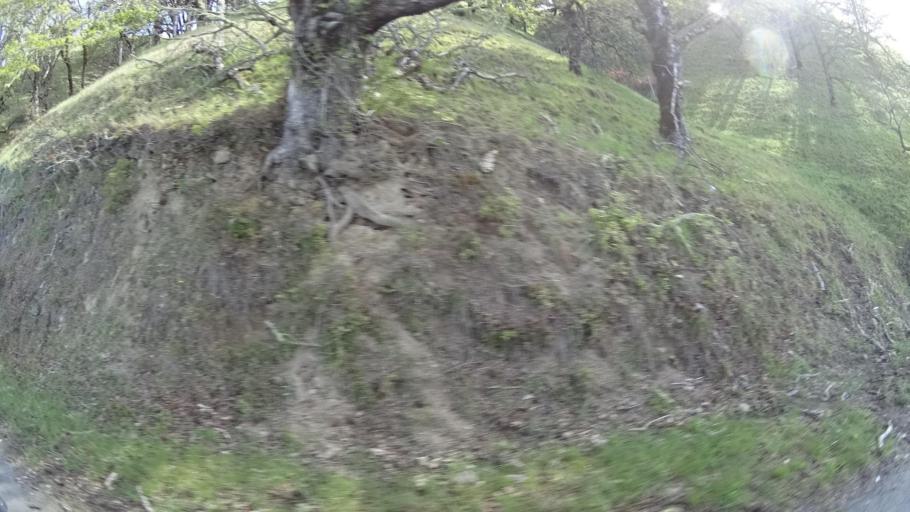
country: US
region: California
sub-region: Humboldt County
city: Hydesville
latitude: 40.6398
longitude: -123.9024
